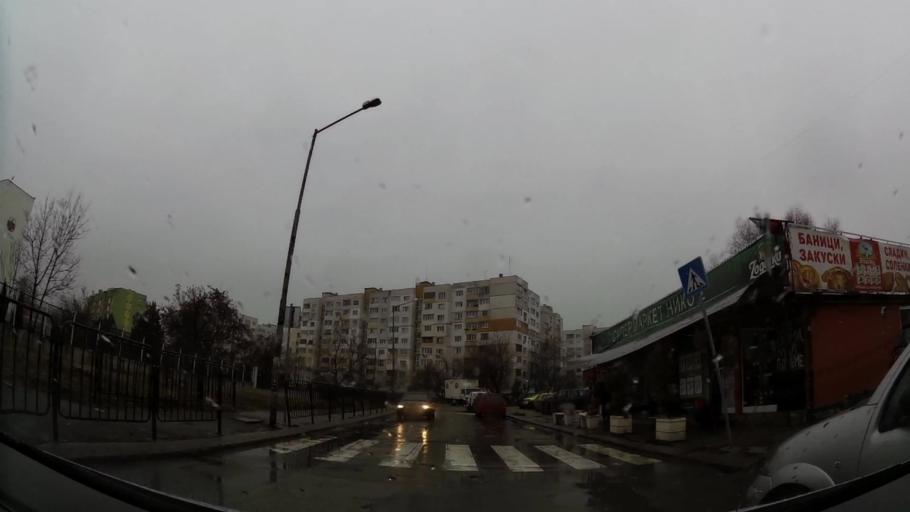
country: BG
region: Sofia-Capital
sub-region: Stolichna Obshtina
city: Sofia
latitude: 42.6461
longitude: 23.4093
